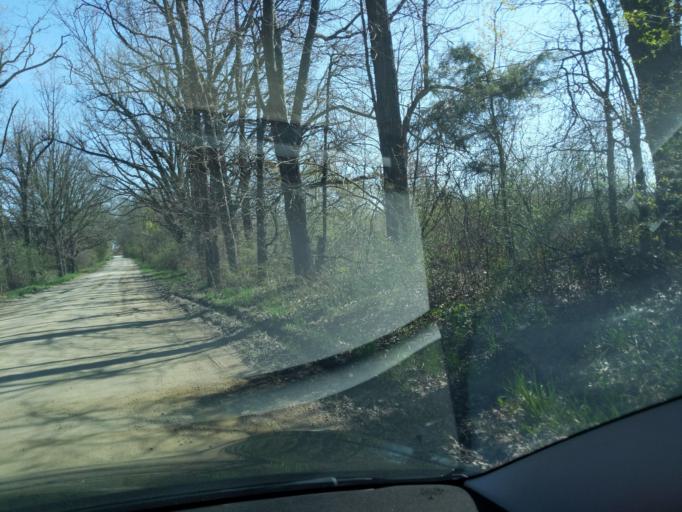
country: US
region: Michigan
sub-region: Ingham County
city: Stockbridge
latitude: 42.4295
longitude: -84.0826
